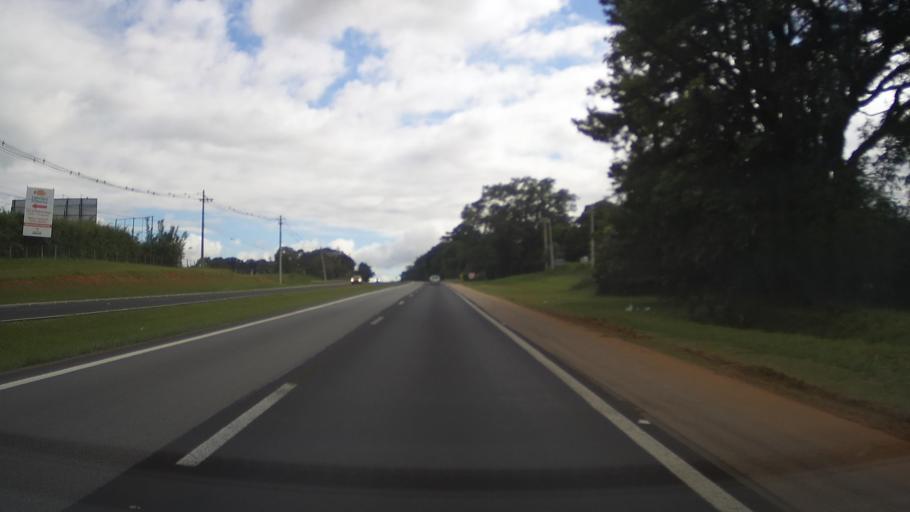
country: BR
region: Sao Paulo
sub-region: Itupeva
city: Itupeva
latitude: -23.2166
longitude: -47.0203
